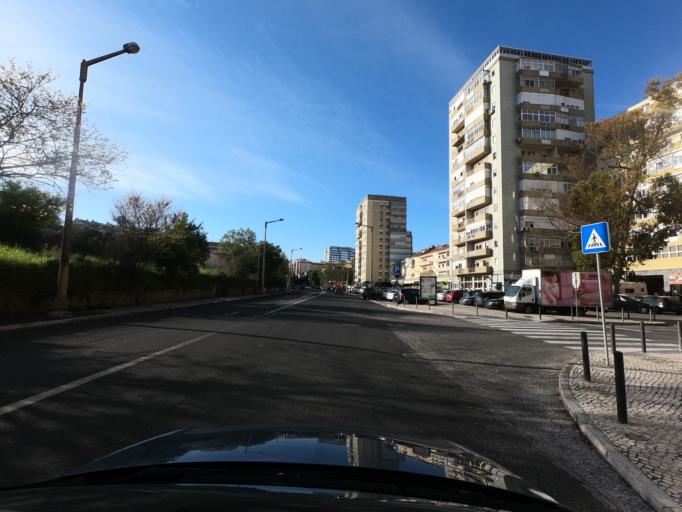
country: PT
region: Lisbon
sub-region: Odivelas
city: Pontinha
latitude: 38.7522
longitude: -9.1738
